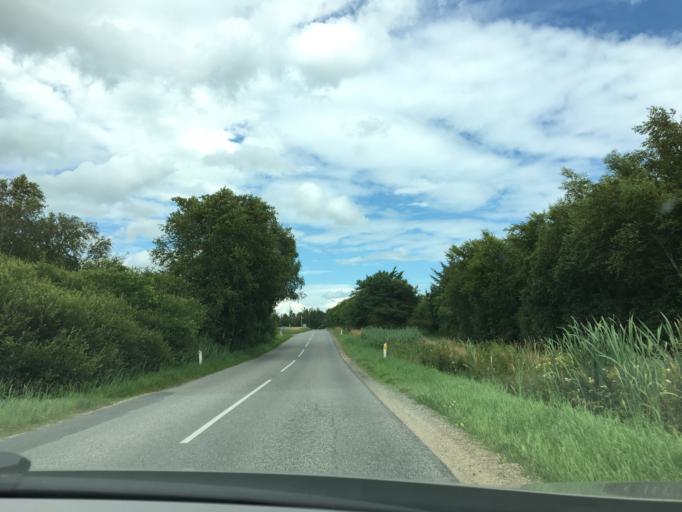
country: DK
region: South Denmark
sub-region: Varde Kommune
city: Oksbol
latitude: 55.6623
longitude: 8.3023
